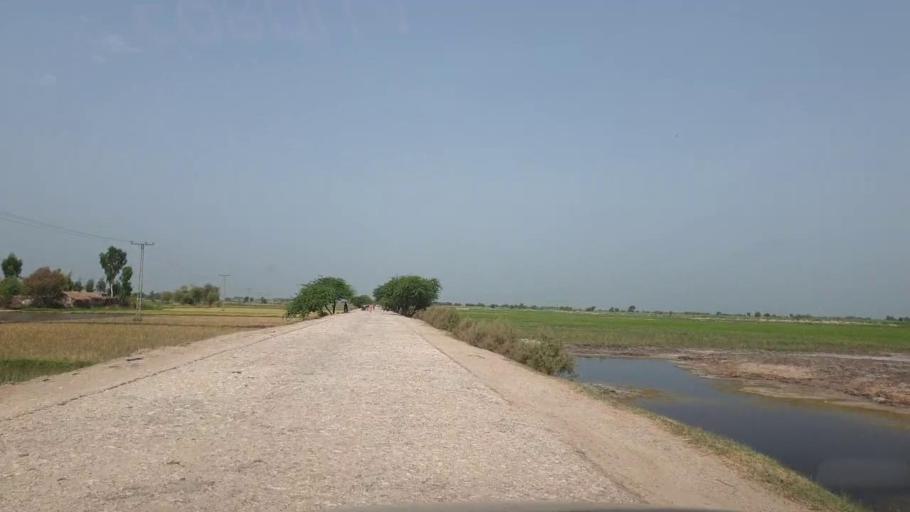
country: PK
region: Sindh
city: Garhi Yasin
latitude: 27.8577
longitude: 68.4141
